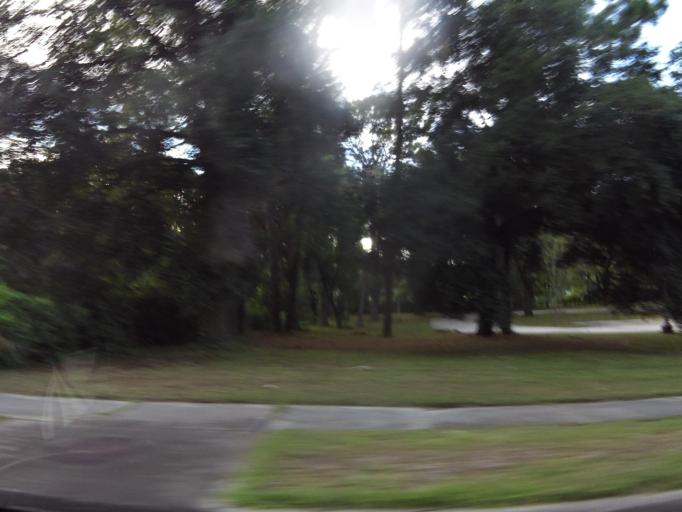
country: US
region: Florida
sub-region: Duval County
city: Jacksonville
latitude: 30.4054
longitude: -81.6983
